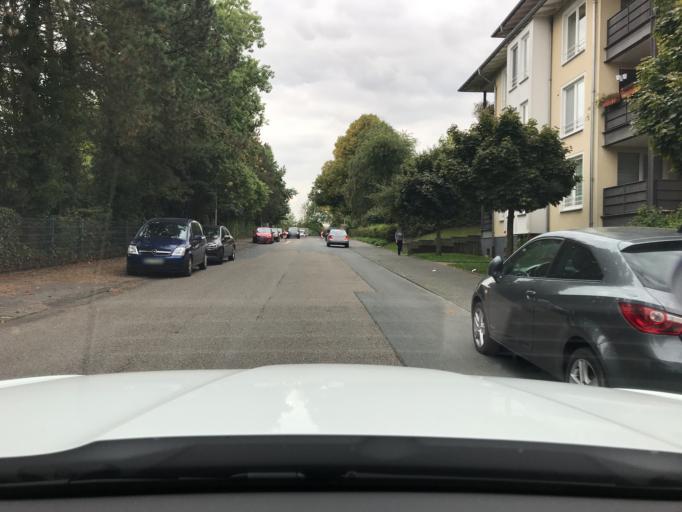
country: DE
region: North Rhine-Westphalia
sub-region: Regierungsbezirk Dusseldorf
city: Muelheim (Ruhr)
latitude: 51.4211
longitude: 6.8667
